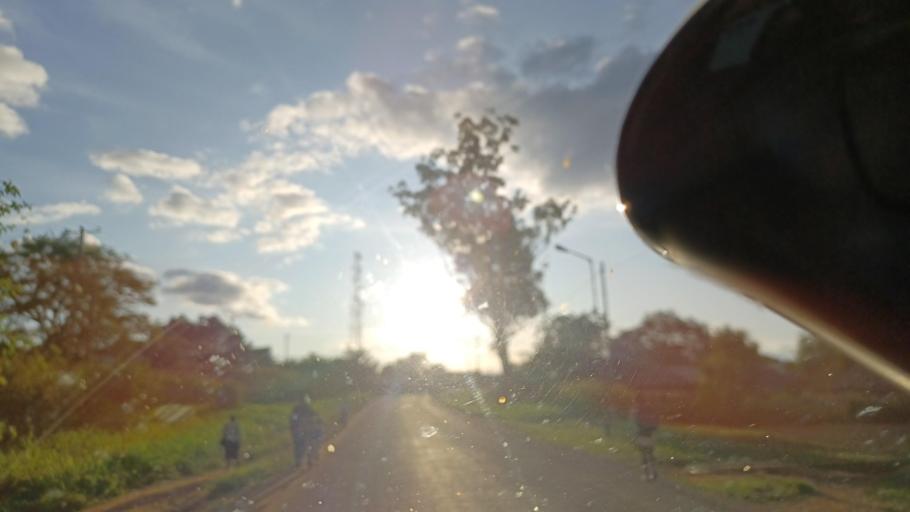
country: ZM
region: North-Western
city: Kasempa
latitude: -13.4591
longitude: 25.8366
